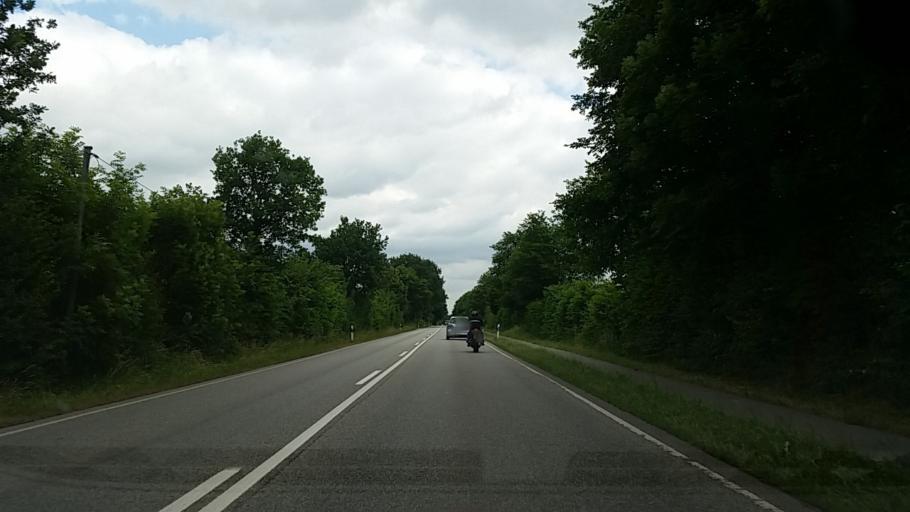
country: DE
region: Schleswig-Holstein
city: Tangstedt
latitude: 53.7235
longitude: 10.0926
